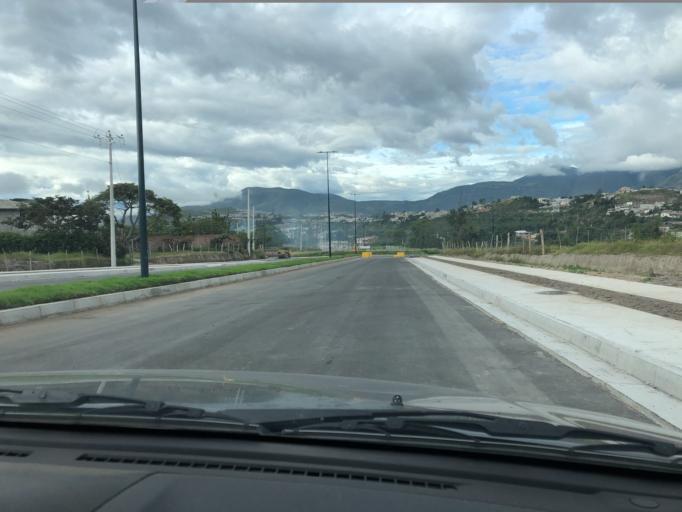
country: EC
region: Imbabura
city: Ibarra
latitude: 0.3393
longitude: -78.1561
